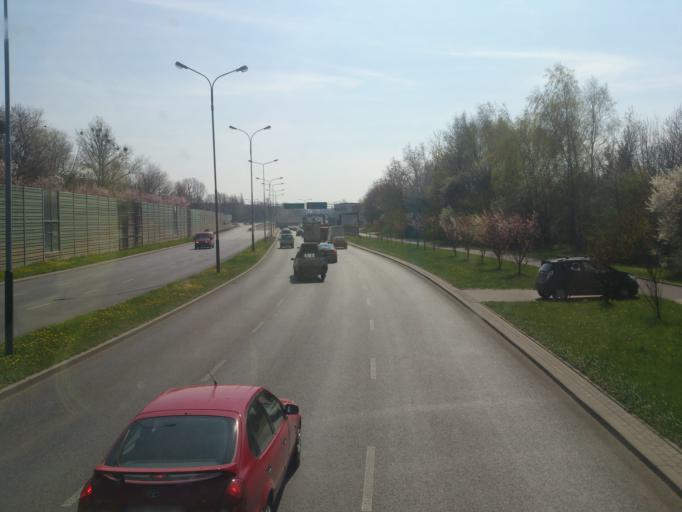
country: PL
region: Lodz Voivodeship
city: Lodz
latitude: 51.7301
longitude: 19.4428
